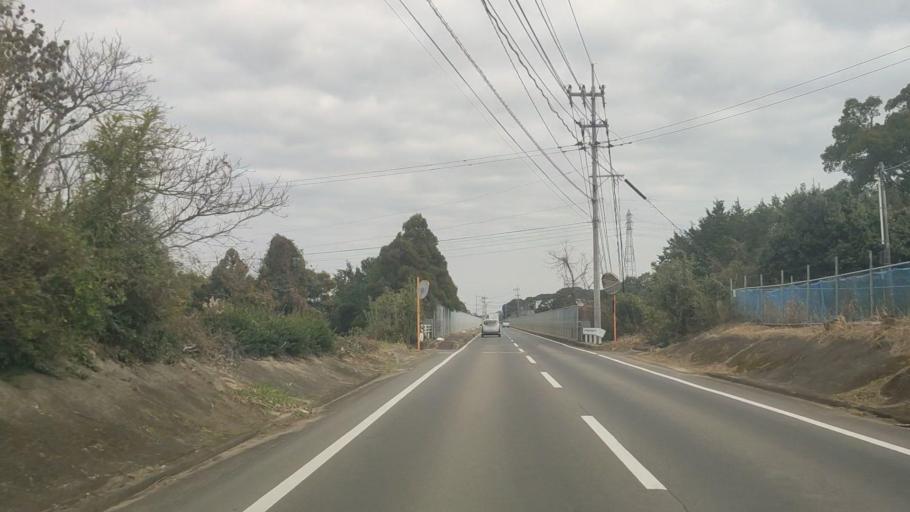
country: JP
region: Nagasaki
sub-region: Isahaya-shi
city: Isahaya
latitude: 32.8062
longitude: 130.1686
